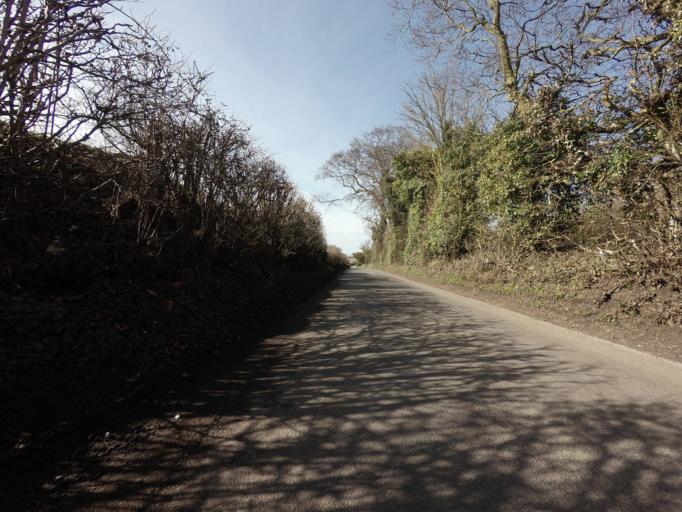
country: GB
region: England
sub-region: Kent
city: Eynsford
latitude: 51.3774
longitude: 0.1944
